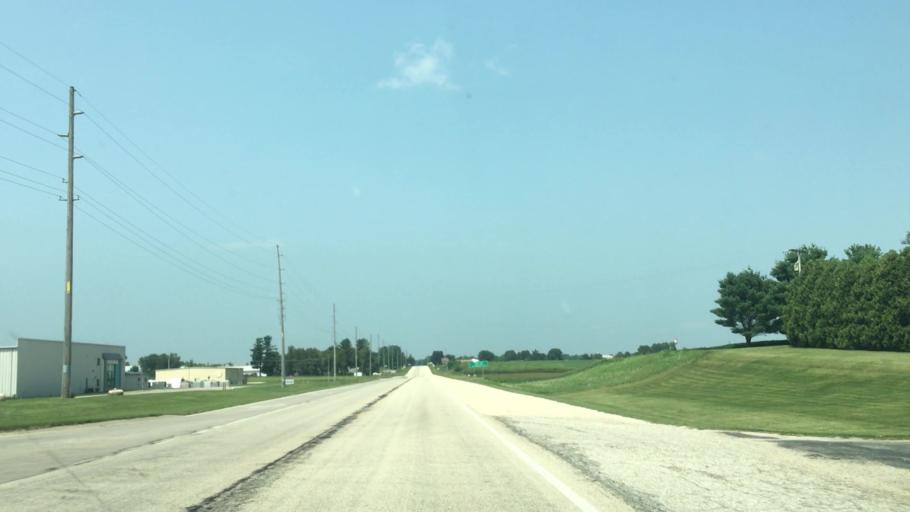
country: US
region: Iowa
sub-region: Fayette County
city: West Union
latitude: 42.9413
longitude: -91.8142
